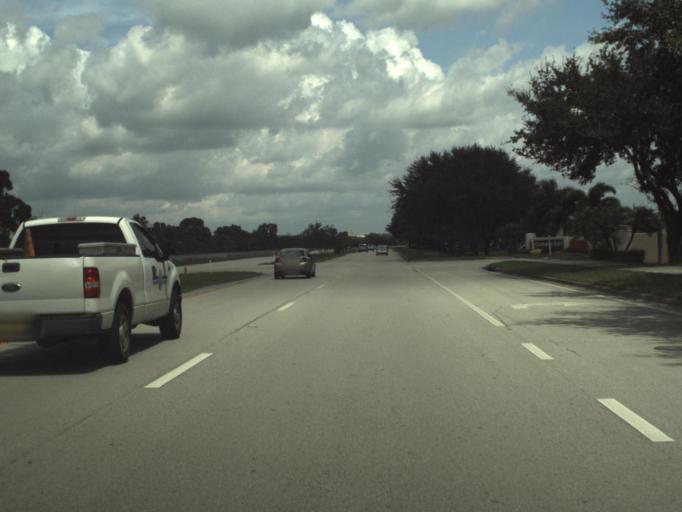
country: US
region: Florida
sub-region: Palm Beach County
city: North Palm Beach
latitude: 26.8236
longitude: -80.0872
